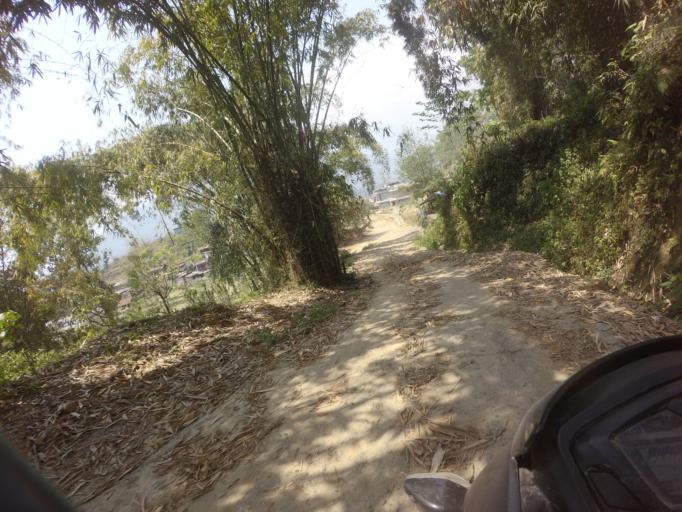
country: NP
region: Western Region
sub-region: Gandaki Zone
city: Pokhara
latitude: 28.3084
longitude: 83.9596
